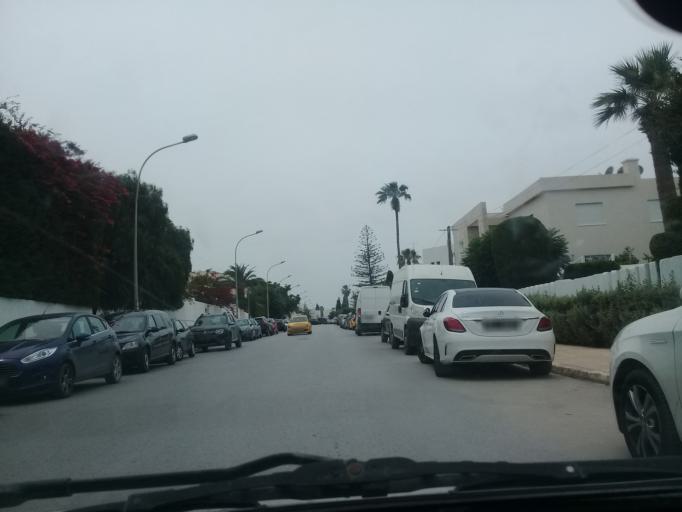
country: TN
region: Tunis
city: Tunis
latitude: 36.8422
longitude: 10.1625
